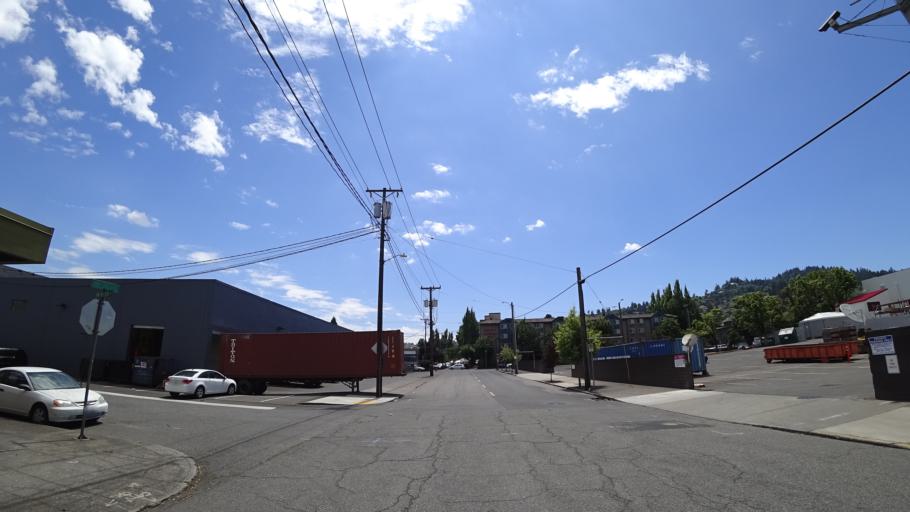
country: US
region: Oregon
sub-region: Multnomah County
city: Portland
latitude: 45.5377
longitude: -122.7009
